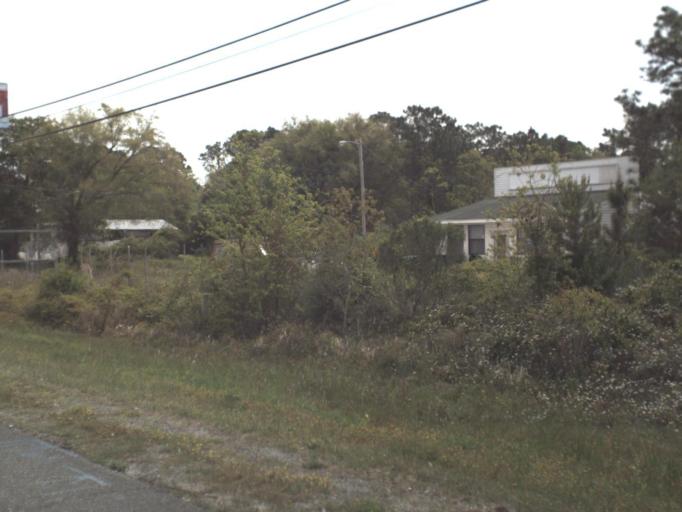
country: US
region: Florida
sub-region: Santa Rosa County
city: Tiger Point
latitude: 30.3950
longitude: -87.0317
